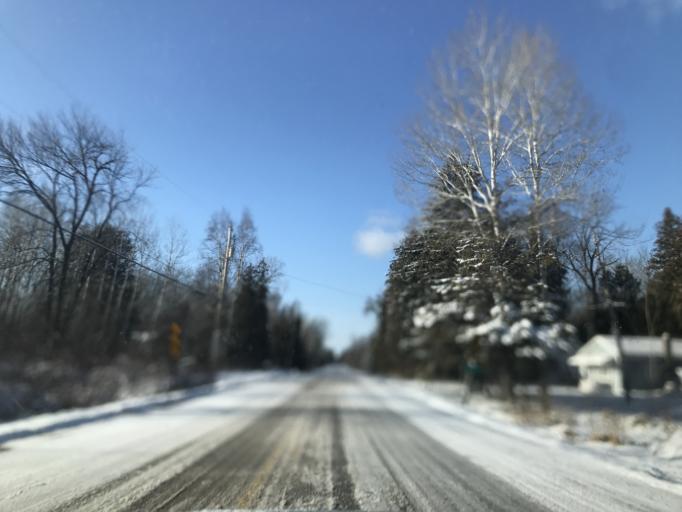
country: US
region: Wisconsin
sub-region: Door County
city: Sturgeon Bay
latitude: 44.8496
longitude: -87.4891
